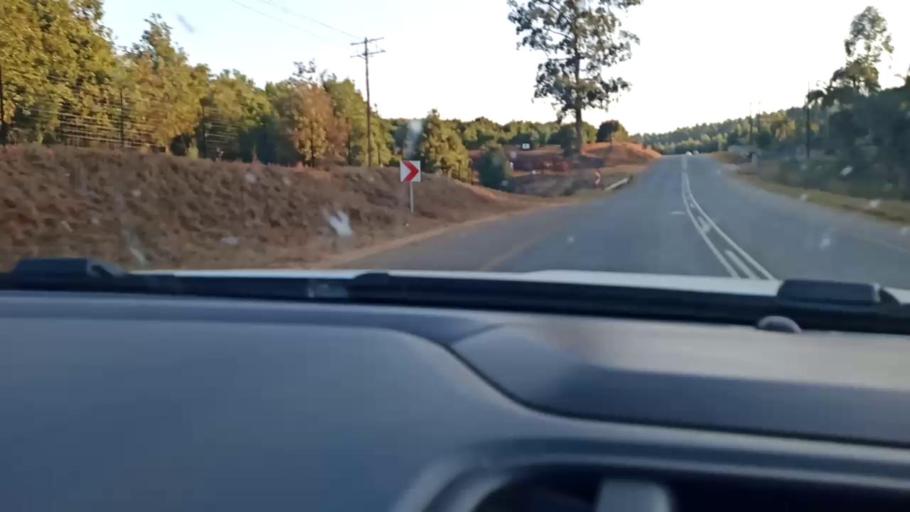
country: ZA
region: Limpopo
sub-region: Mopani District Municipality
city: Duiwelskloof
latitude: -23.7124
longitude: 30.1292
